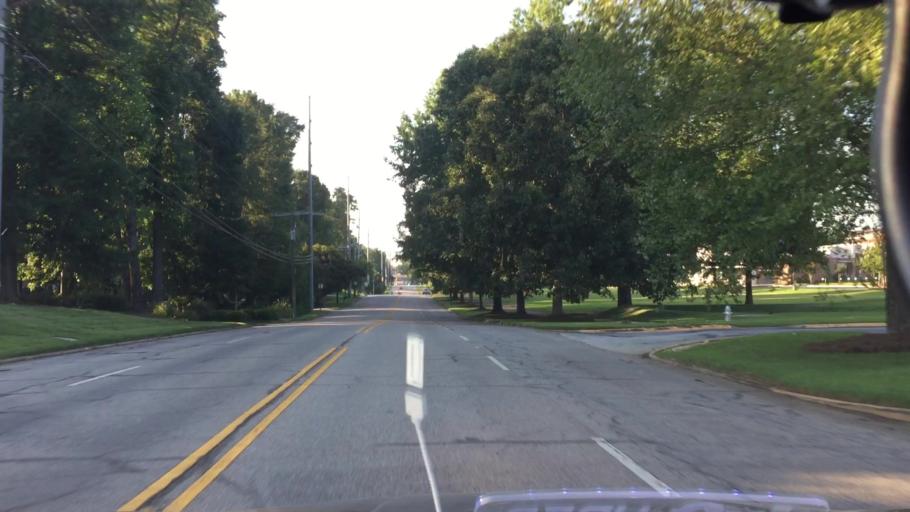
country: US
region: Alabama
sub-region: Lee County
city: Auburn
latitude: 32.5961
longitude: -85.4648
